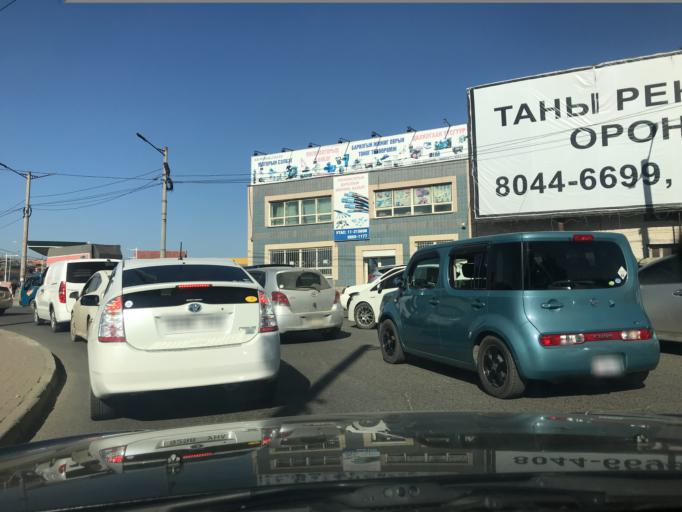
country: MN
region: Ulaanbaatar
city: Ulaanbaatar
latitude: 47.9284
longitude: 106.9057
